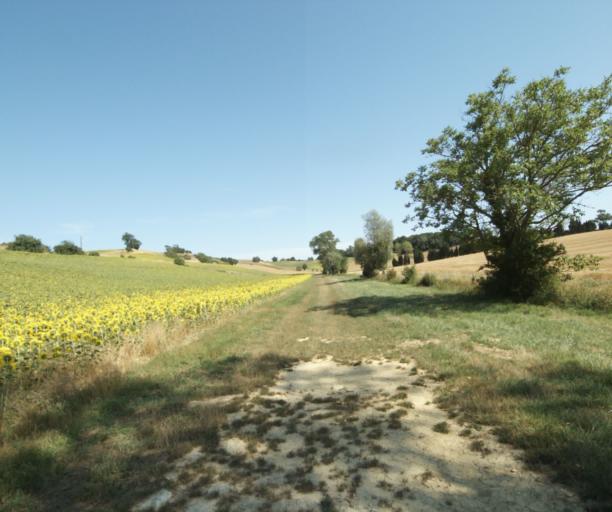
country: FR
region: Midi-Pyrenees
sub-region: Departement de la Haute-Garonne
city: Saint-Felix-Lauragais
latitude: 43.4366
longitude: 1.8473
